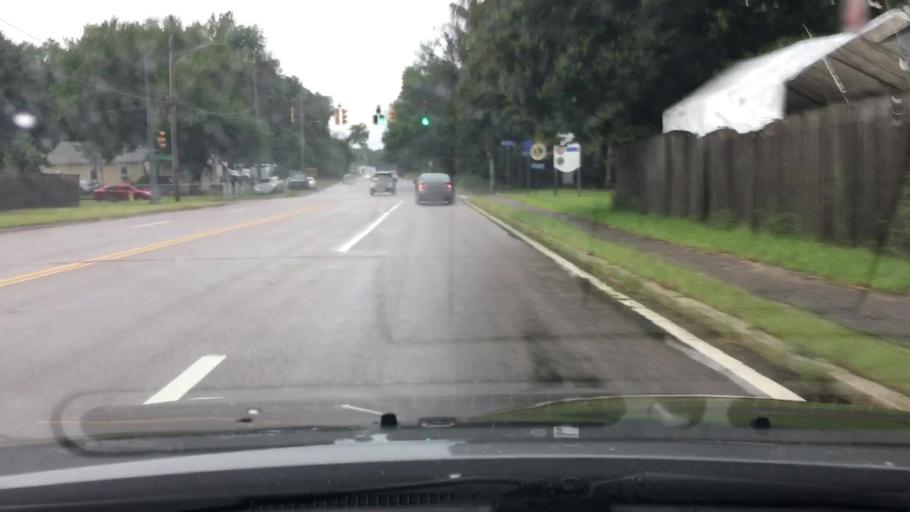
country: US
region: Rhode Island
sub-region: Providence County
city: Valley Falls
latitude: 41.9095
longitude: -71.3578
